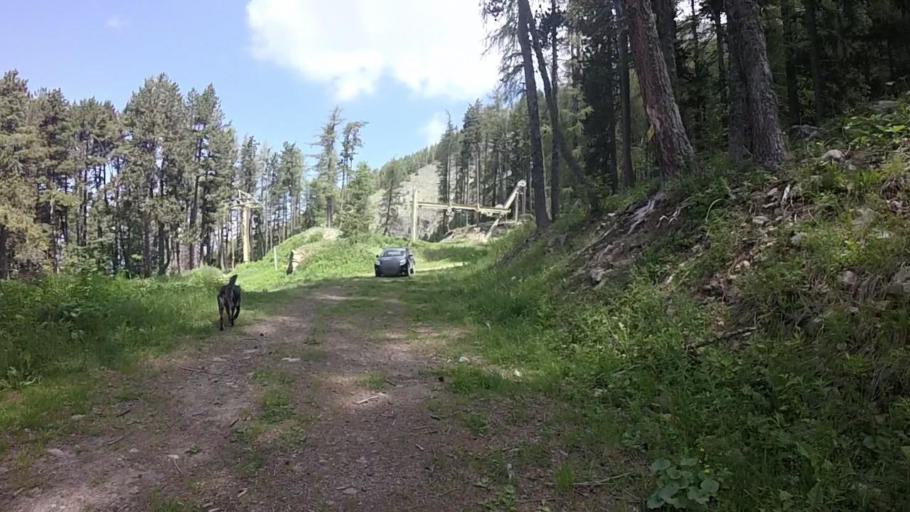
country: FR
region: Provence-Alpes-Cote d'Azur
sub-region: Departement des Alpes-de-Haute-Provence
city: Seyne-les-Alpes
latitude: 44.4041
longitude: 6.3753
